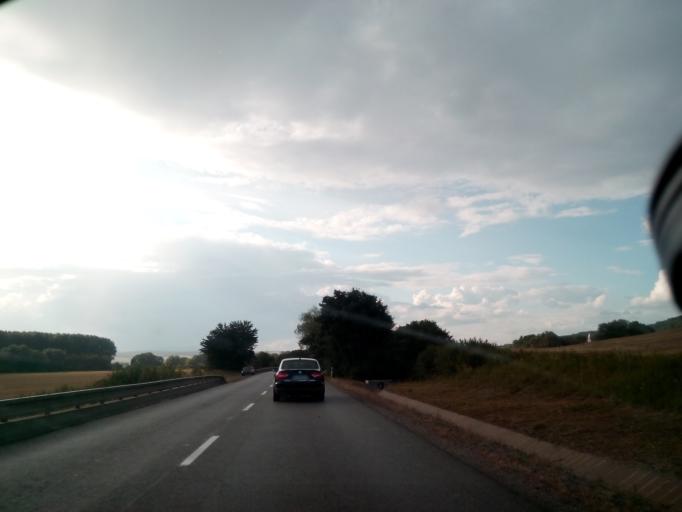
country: SK
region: Kosicky
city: Kosice
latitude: 48.6503
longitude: 21.3614
